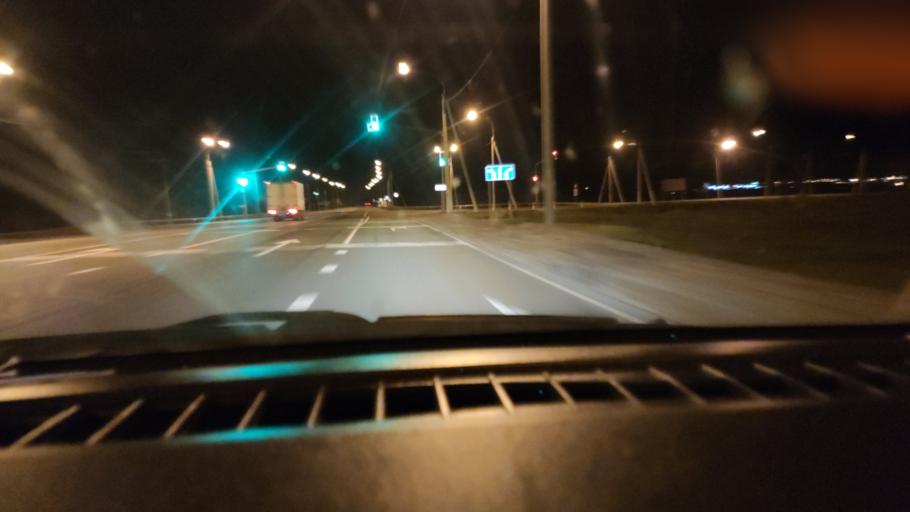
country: RU
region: Samara
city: Syzran'
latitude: 53.2079
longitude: 48.5078
